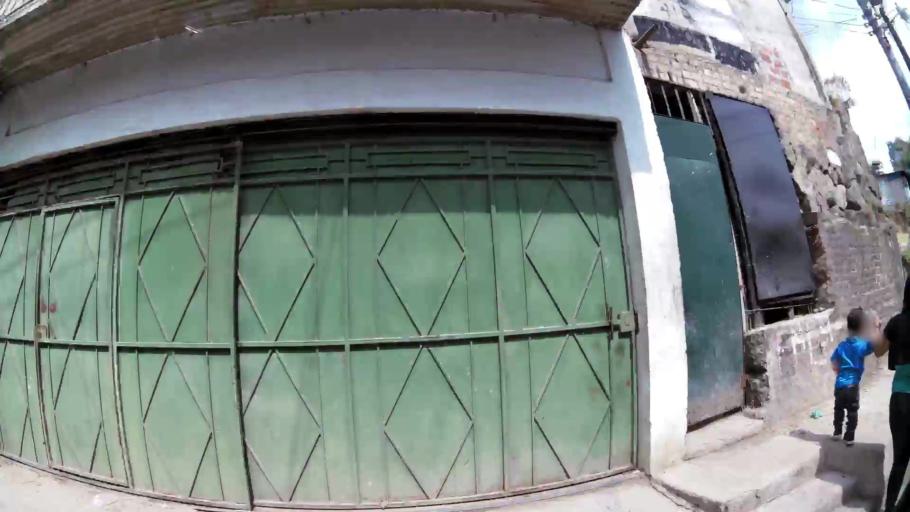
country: SV
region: San Salvador
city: Mejicanos
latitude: 13.7158
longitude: -89.2359
